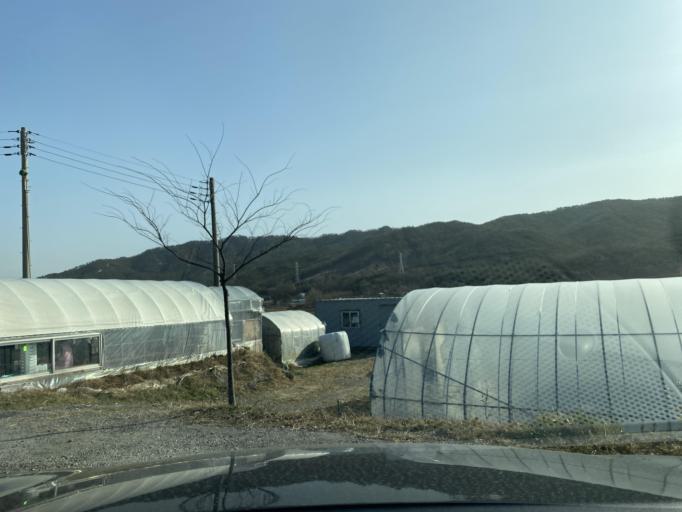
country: KR
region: Chungcheongnam-do
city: Hongsung
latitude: 36.6791
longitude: 126.6456
